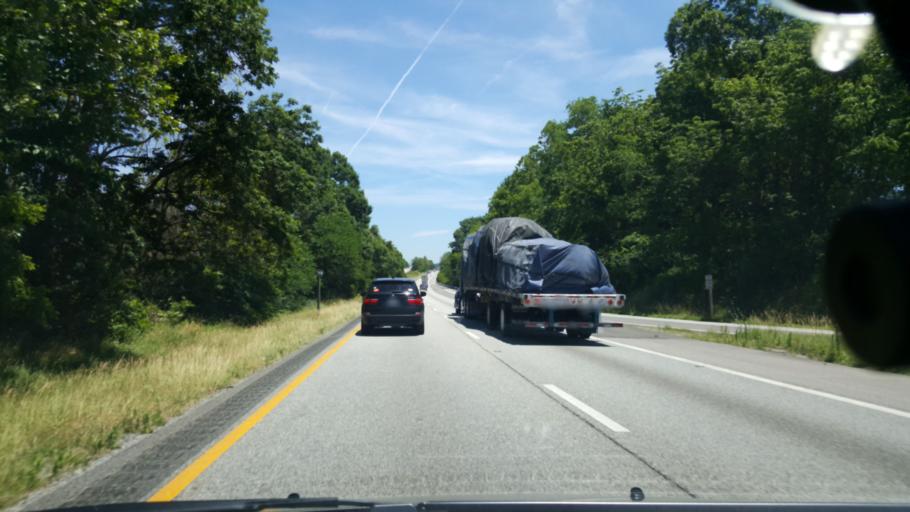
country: US
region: Virginia
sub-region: Botetourt County
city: Fincastle
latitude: 37.4578
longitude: -79.8366
